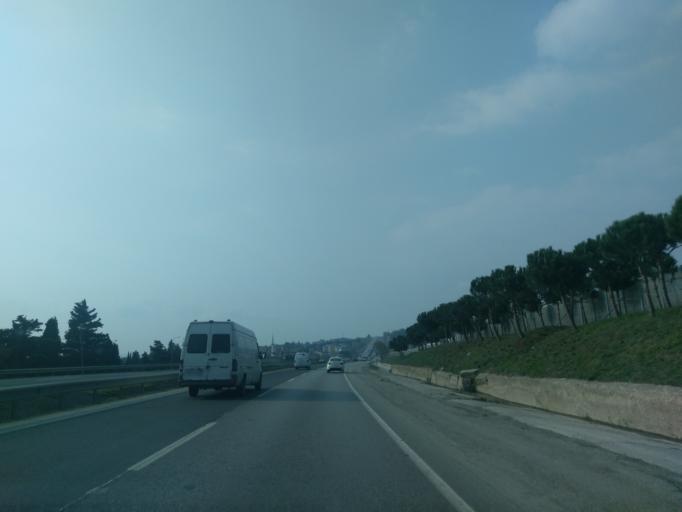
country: TR
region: Istanbul
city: Kumburgaz
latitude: 41.0081
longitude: 28.5063
